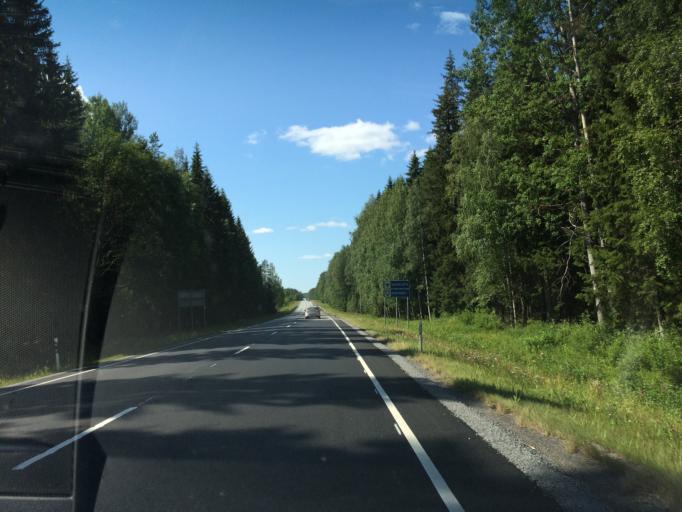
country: FI
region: Pirkanmaa
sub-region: Lounais-Pirkanmaa
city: Kiikoinen
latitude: 61.4758
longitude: 22.4528
